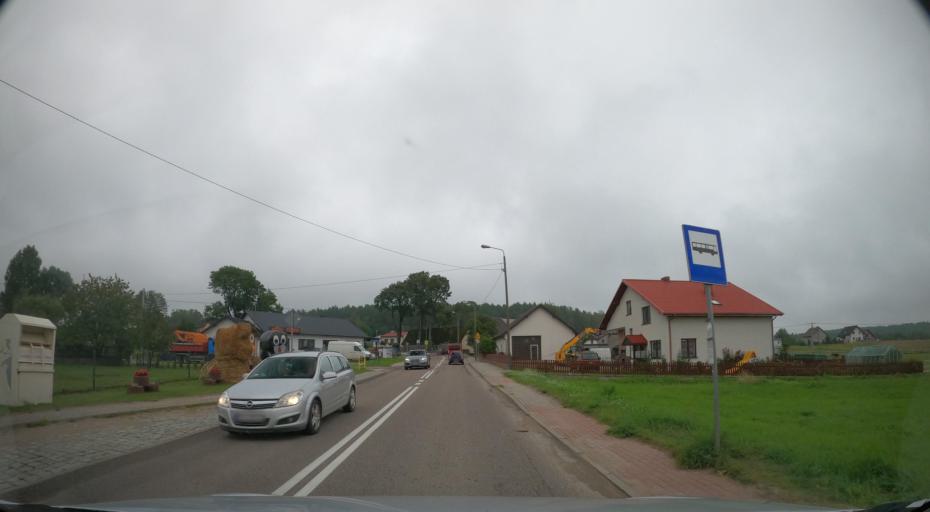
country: PL
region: Pomeranian Voivodeship
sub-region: Powiat wejherowski
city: Luzino
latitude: 54.4683
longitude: 18.0715
